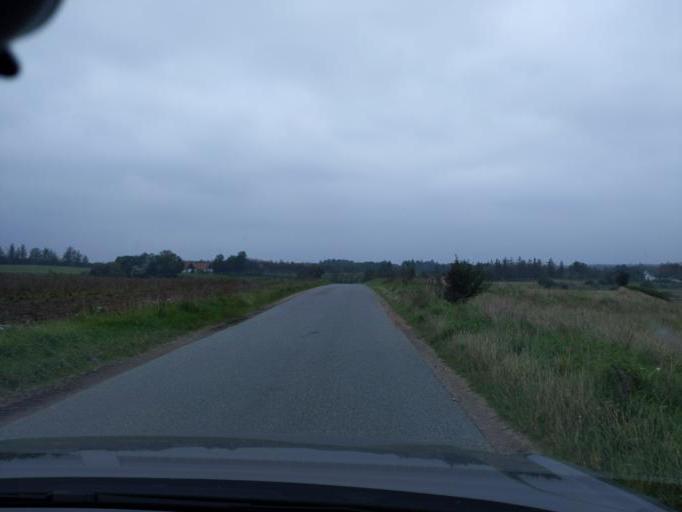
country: DK
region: Central Jutland
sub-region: Viborg Kommune
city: Stoholm
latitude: 56.5011
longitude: 9.2463
